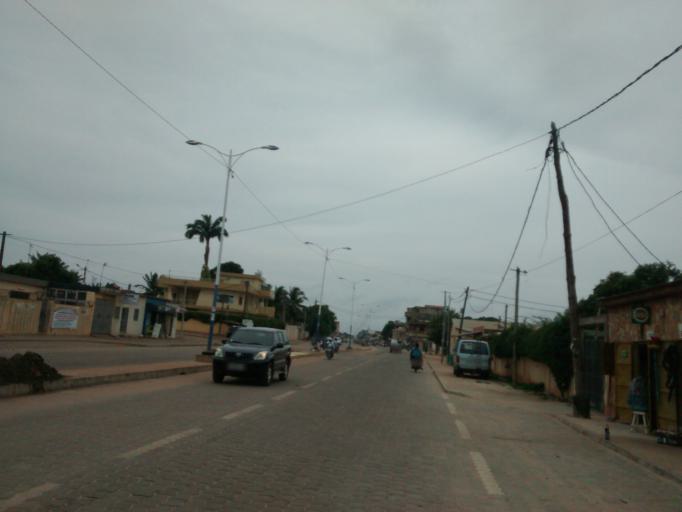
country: TG
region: Maritime
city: Lome
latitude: 6.1740
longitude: 1.1984
